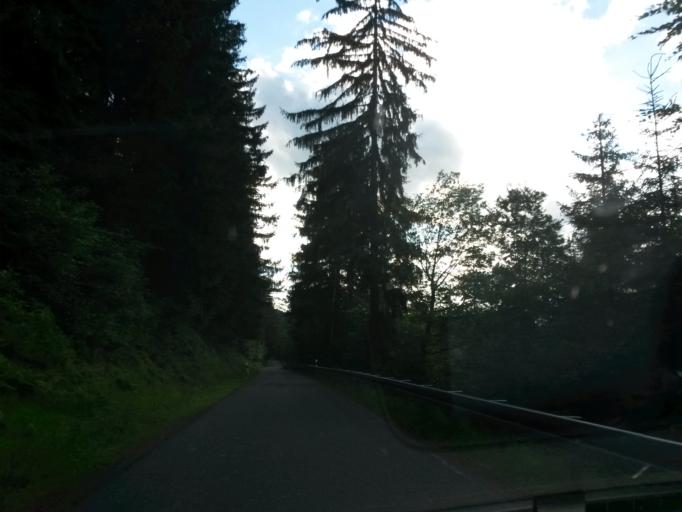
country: DE
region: North Rhine-Westphalia
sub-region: Regierungsbezirk Arnsberg
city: Herscheid
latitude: 51.1019
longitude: 7.7386
